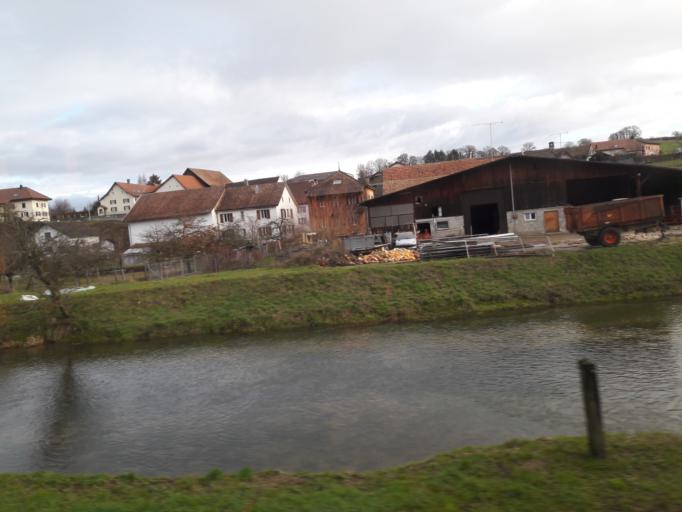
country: CH
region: Jura
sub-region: Porrentruy District
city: Boncourt
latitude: 47.4799
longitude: 7.0296
